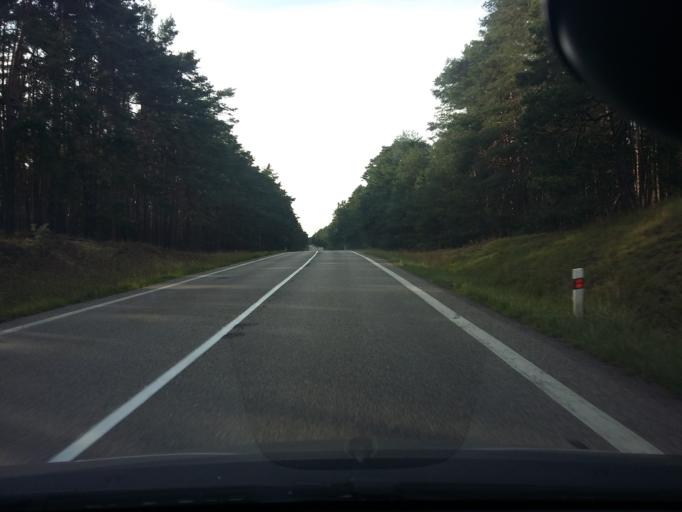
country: SK
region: Bratislavsky
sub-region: Okres Malacky
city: Malacky
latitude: 48.3938
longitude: 17.0941
